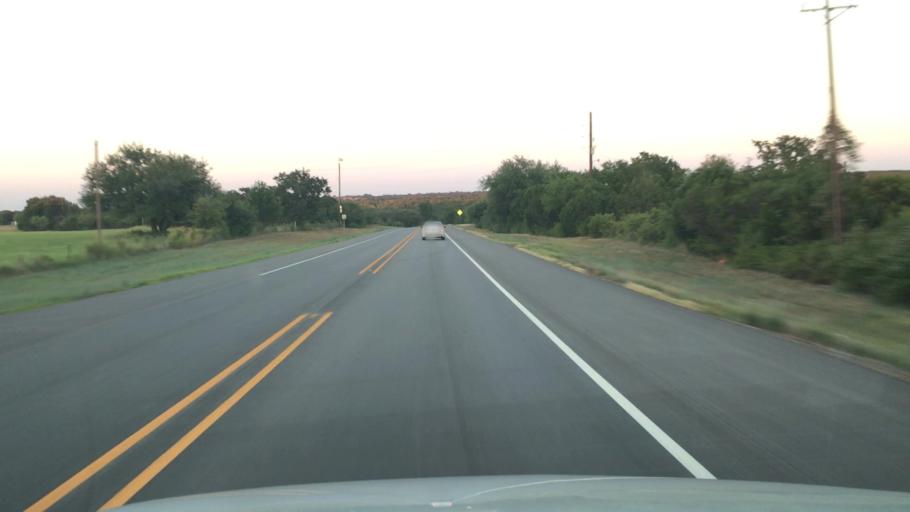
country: US
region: Texas
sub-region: Somervell County
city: Glen Rose
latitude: 32.1911
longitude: -97.8307
